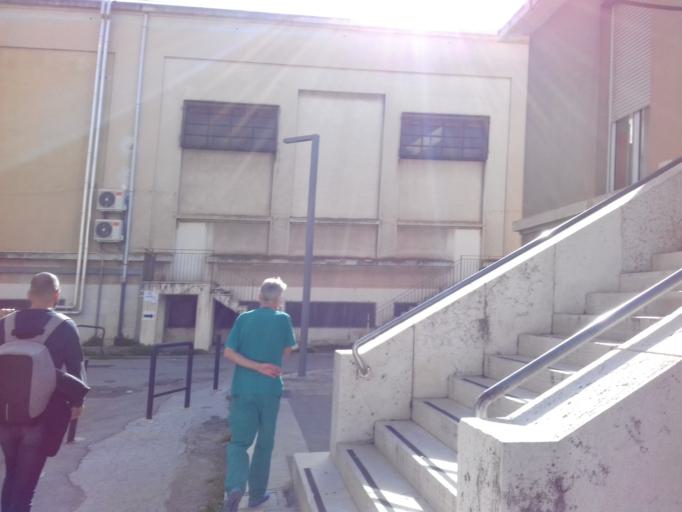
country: IT
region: Apulia
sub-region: Provincia di Bari
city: Bari
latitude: 41.1128
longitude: 16.8601
